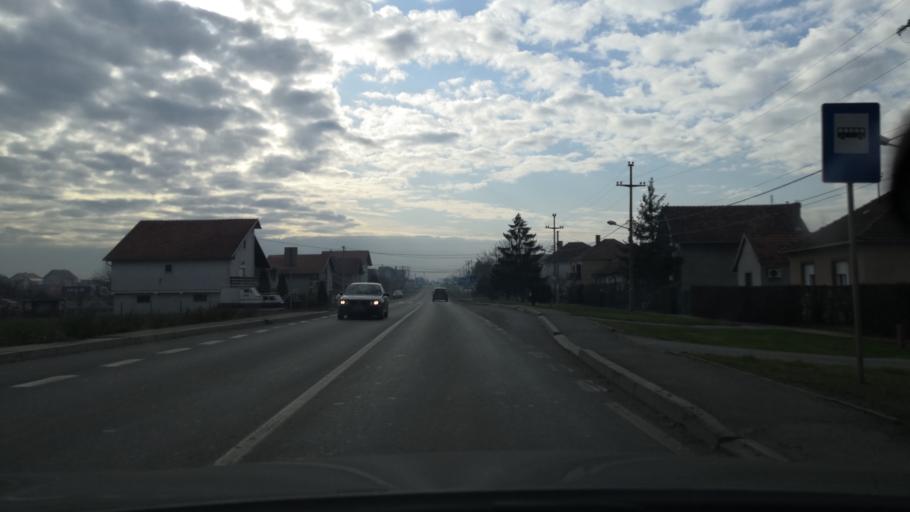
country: RS
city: Ugrinovci
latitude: 44.8699
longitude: 20.2041
